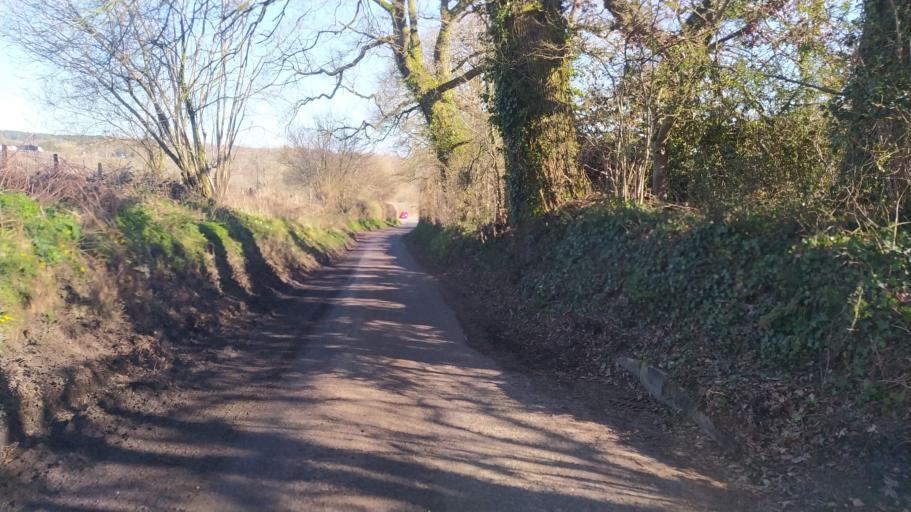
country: GB
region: England
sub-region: Dorset
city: Verwood
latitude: 50.8982
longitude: -1.8971
